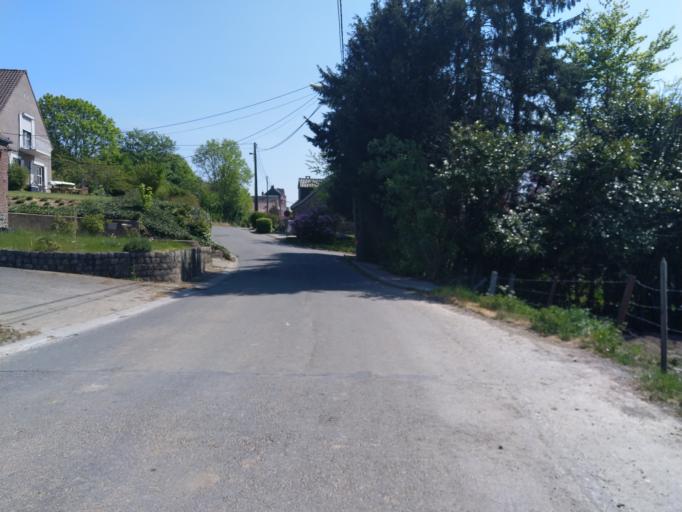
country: BE
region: Wallonia
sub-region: Province du Brabant Wallon
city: Rebecq-Rognon
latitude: 50.6281
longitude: 4.0845
